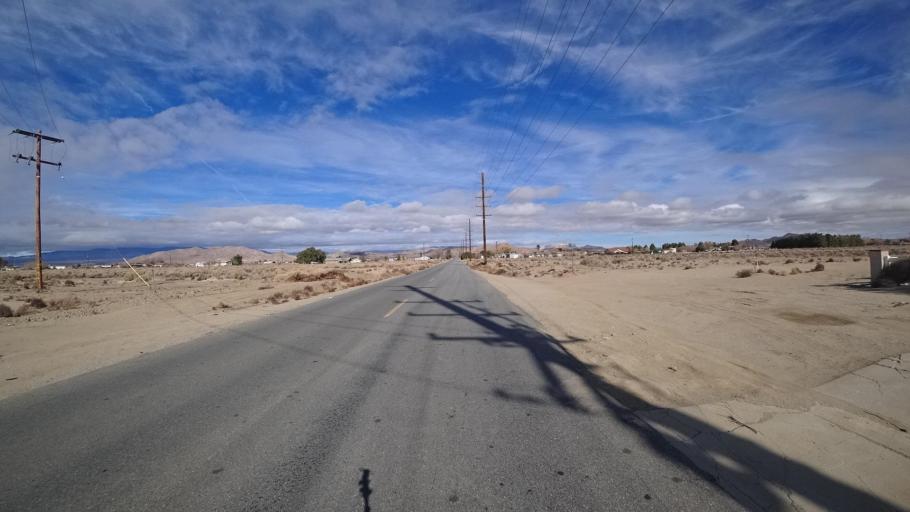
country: US
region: California
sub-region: Kern County
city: Rosamond
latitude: 34.8398
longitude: -118.2378
